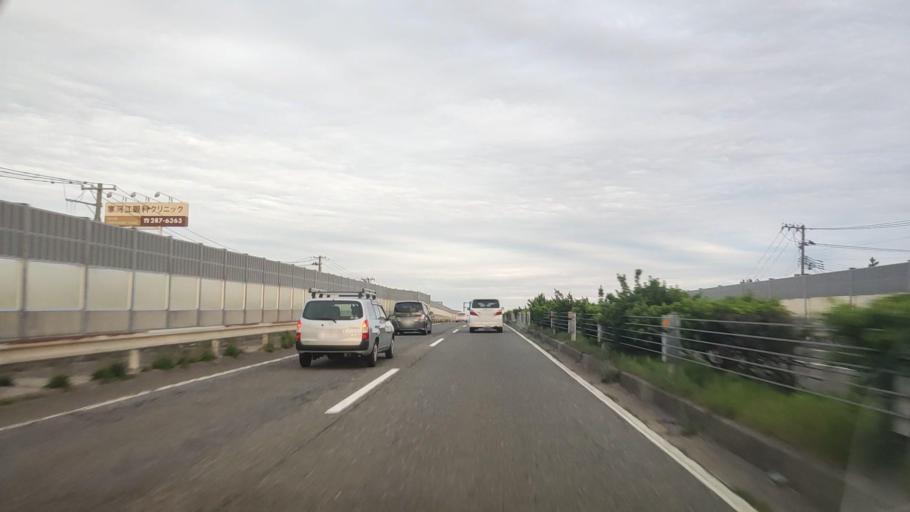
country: JP
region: Niigata
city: Kameda-honcho
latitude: 37.8900
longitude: 139.0756
